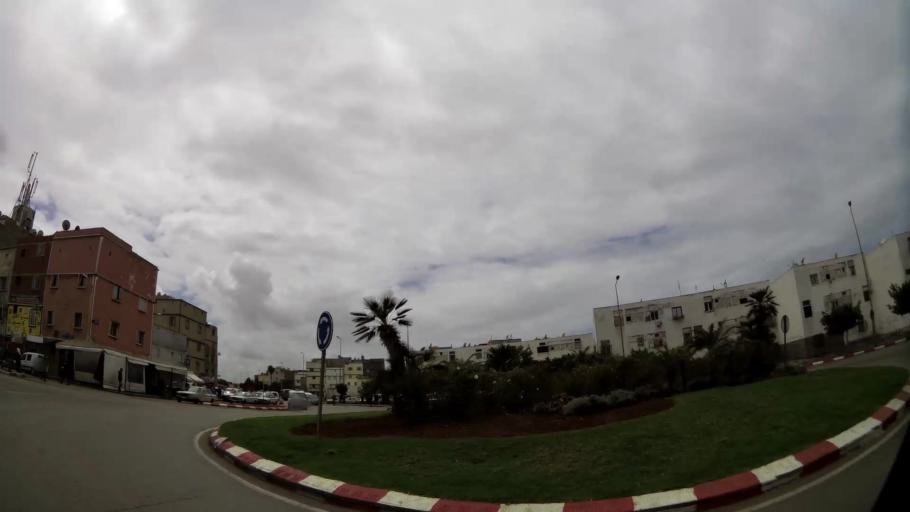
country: MA
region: Grand Casablanca
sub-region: Mediouna
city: Tit Mellil
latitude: 33.6142
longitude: -7.5037
